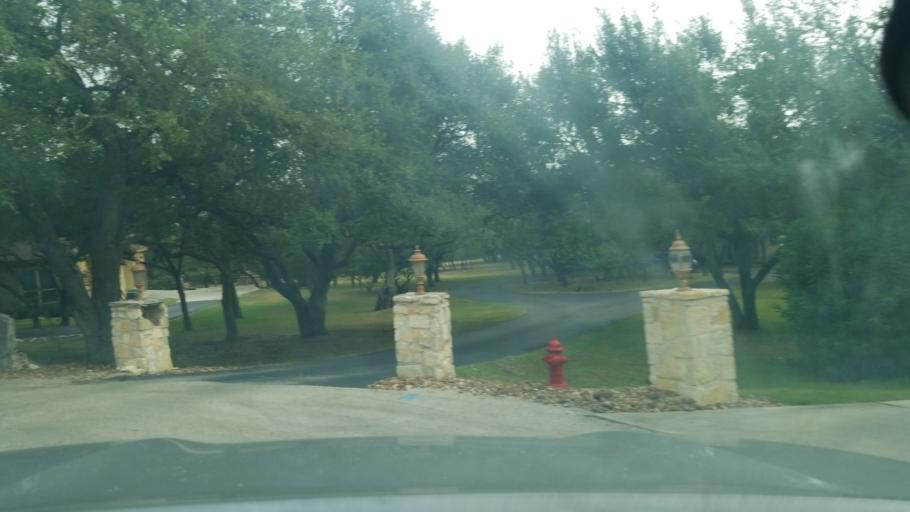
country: US
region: Texas
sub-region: Comal County
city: Bulverde
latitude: 29.8257
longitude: -98.4048
